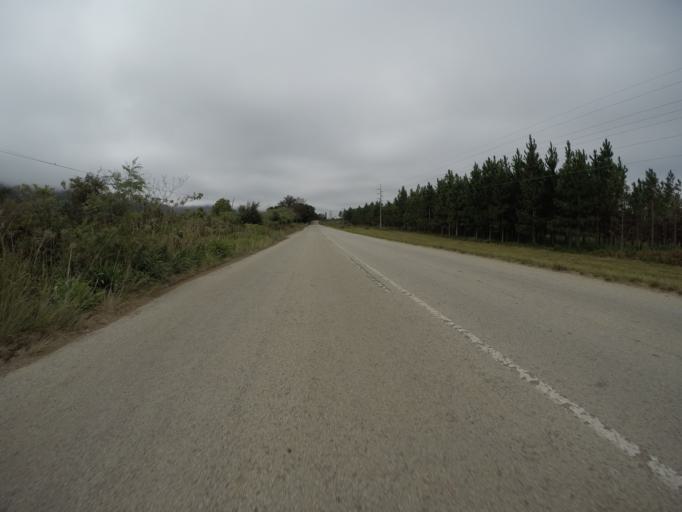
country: ZA
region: Eastern Cape
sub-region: Cacadu District Municipality
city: Kareedouw
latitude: -33.9965
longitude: 24.1423
